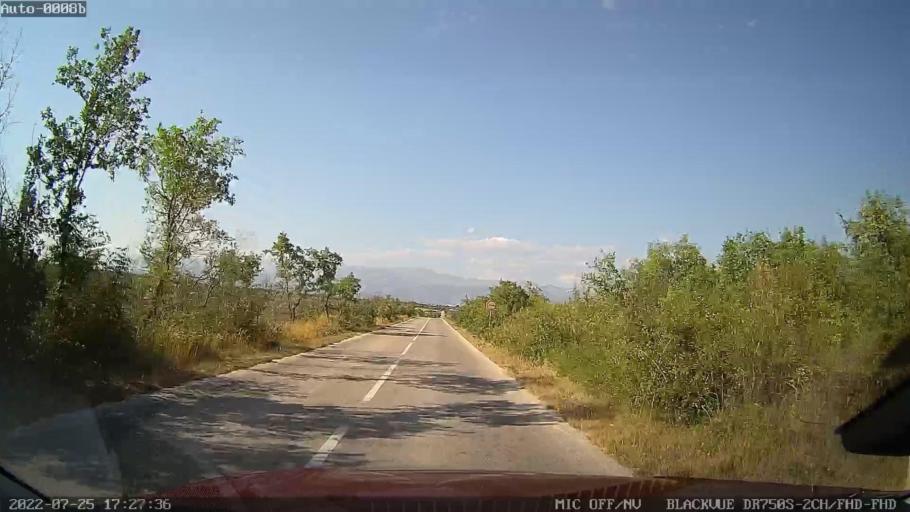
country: HR
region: Zadarska
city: Pridraga
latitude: 44.1449
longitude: 15.5055
